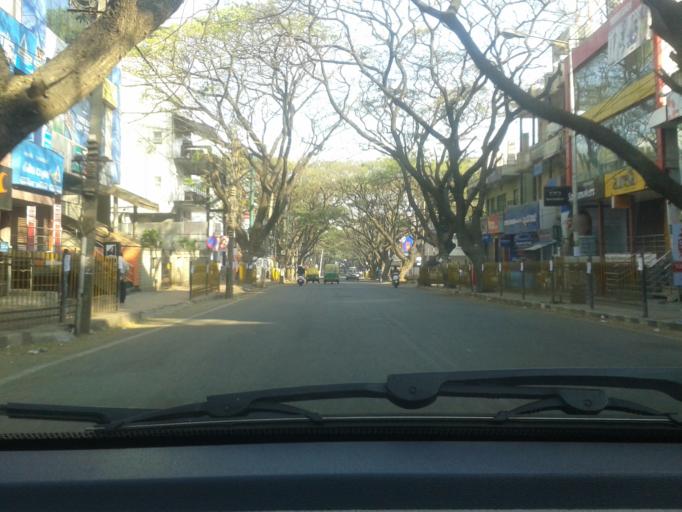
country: IN
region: Karnataka
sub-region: Bangalore Urban
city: Bangalore
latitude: 13.0296
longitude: 77.5708
